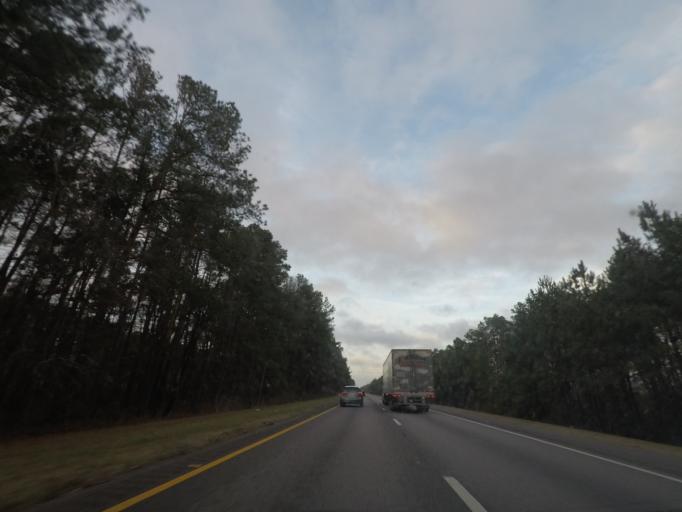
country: US
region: South Carolina
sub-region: Orangeburg County
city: Holly Hill
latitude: 33.3302
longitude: -80.5397
